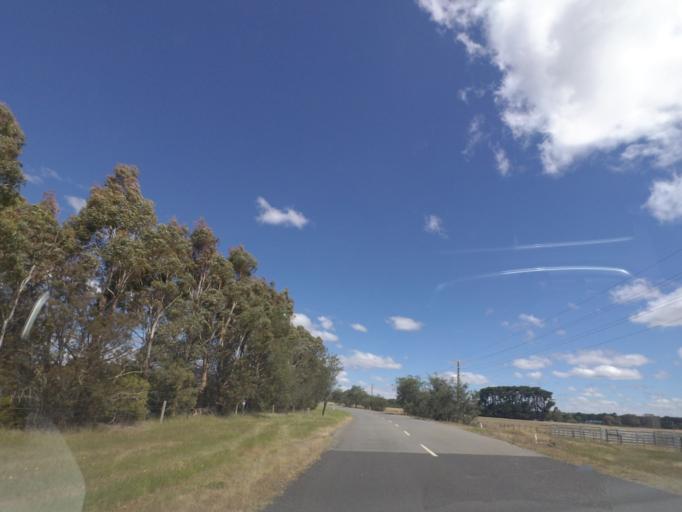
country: AU
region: Victoria
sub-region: Hume
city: Sunbury
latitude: -37.3165
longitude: 144.5205
